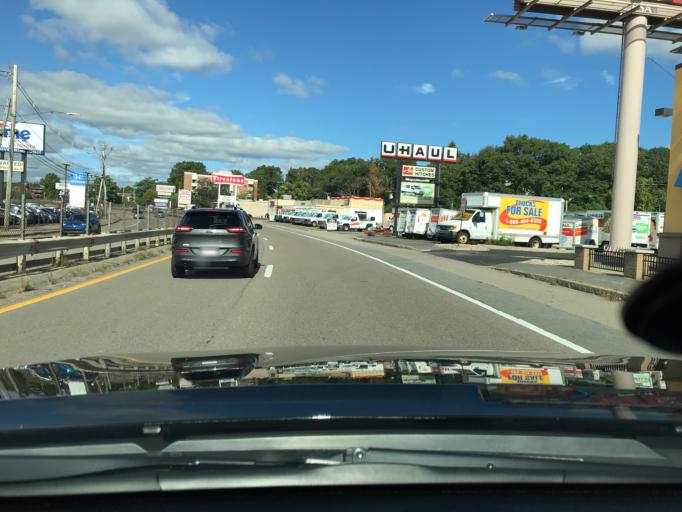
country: US
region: Massachusetts
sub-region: Norfolk County
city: Dedham
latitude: 42.2667
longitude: -71.1688
